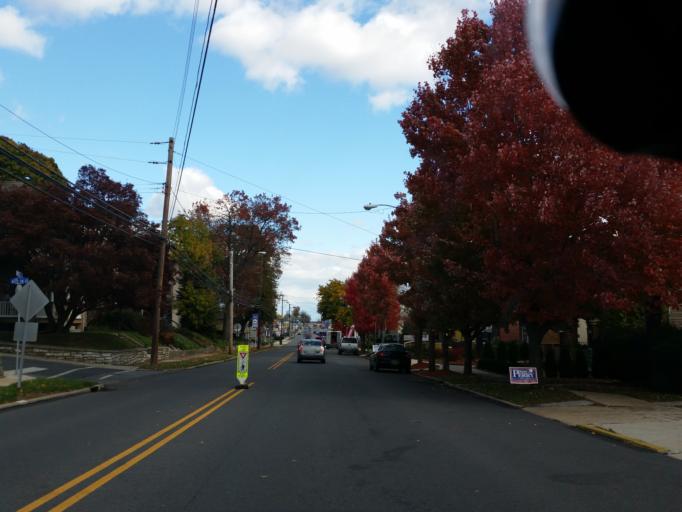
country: US
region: Pennsylvania
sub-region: Cumberland County
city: Camp Hill
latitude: 40.2406
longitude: -76.9115
